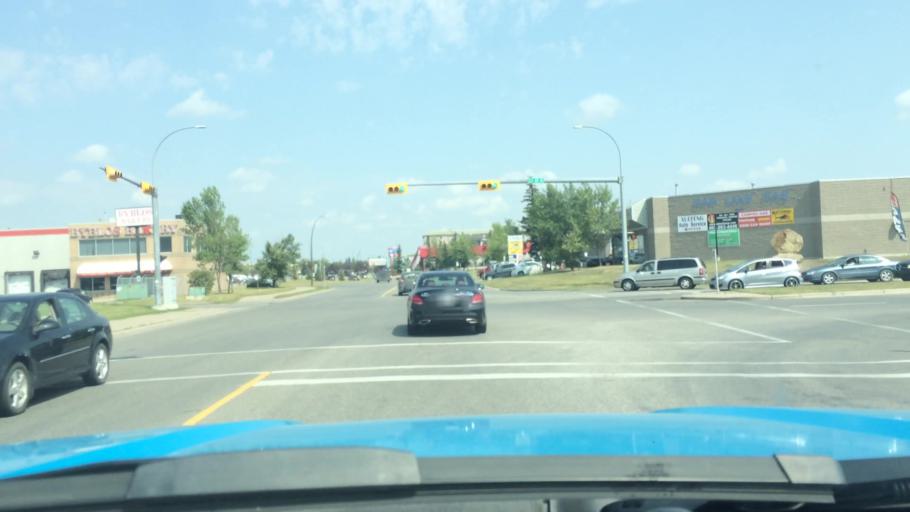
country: CA
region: Alberta
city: Calgary
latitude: 51.0731
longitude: -114.0041
